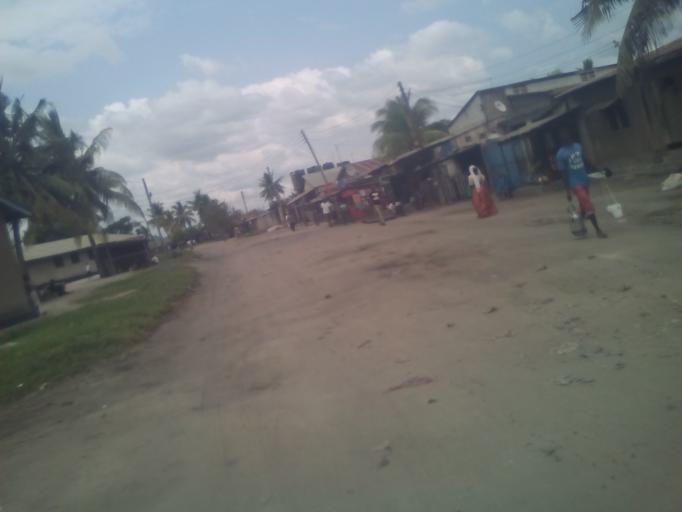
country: TZ
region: Dar es Salaam
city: Dar es Salaam
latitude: -6.8642
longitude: 39.2247
